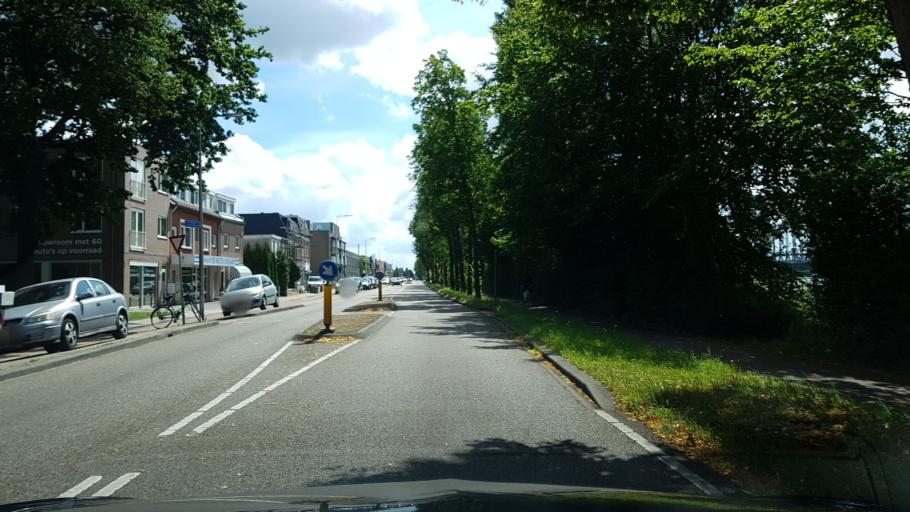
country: NL
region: Utrecht
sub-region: Stichtse Vecht
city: Maarssen
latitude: 52.1156
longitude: 5.0741
